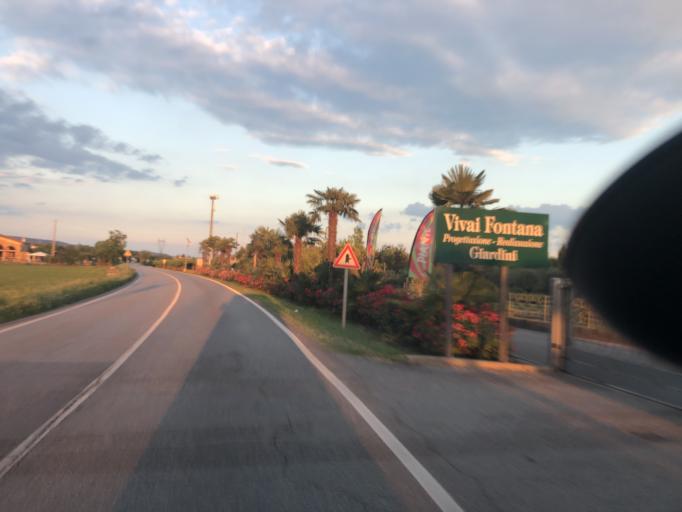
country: IT
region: Veneto
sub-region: Provincia di Verona
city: Pescantina
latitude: 45.4918
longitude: 10.8822
